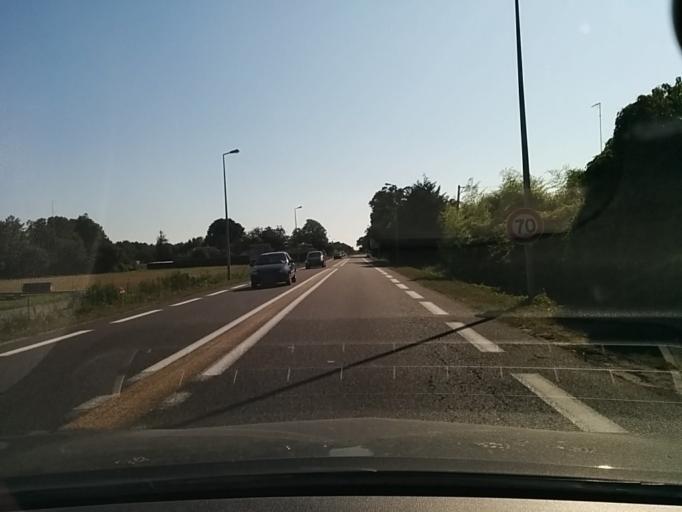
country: FR
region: Aquitaine
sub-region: Departement des Landes
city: Benesse-Maremne
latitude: 43.6295
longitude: -1.3684
